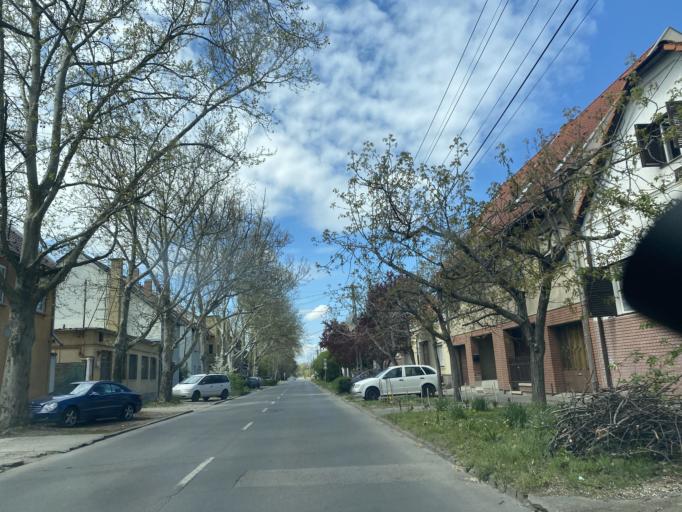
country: HU
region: Csongrad
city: Szeged
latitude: 46.2432
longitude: 20.1345
